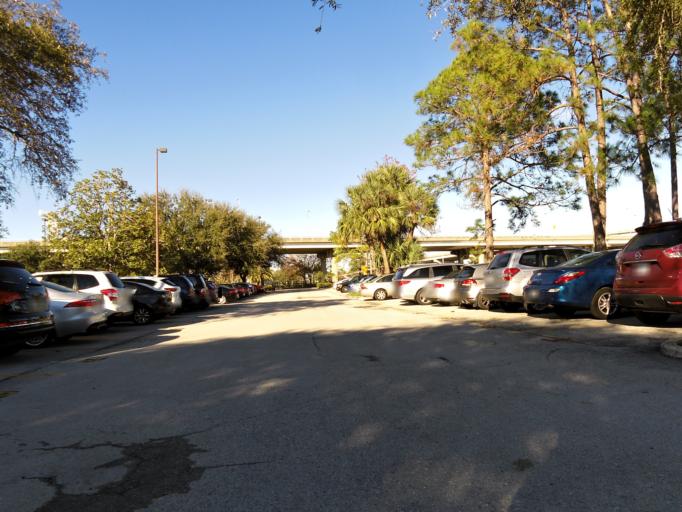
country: US
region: Florida
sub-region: Duval County
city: Jacksonville
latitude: 30.3199
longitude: -81.6361
